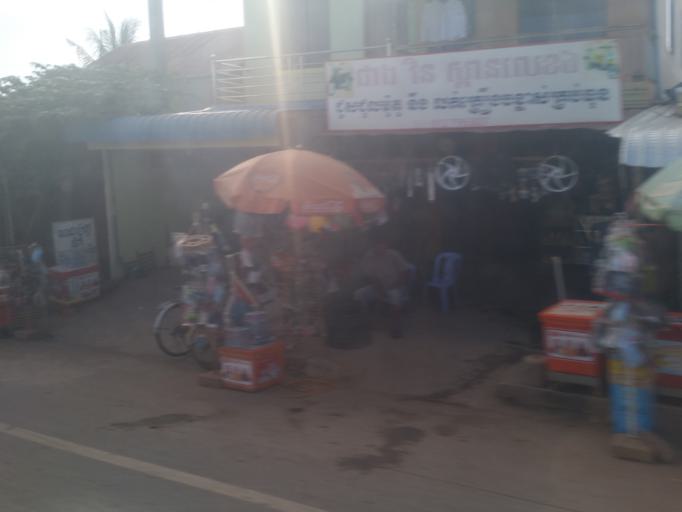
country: KH
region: Phnom Penh
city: Phnom Penh
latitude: 11.6762
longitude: 104.9173
